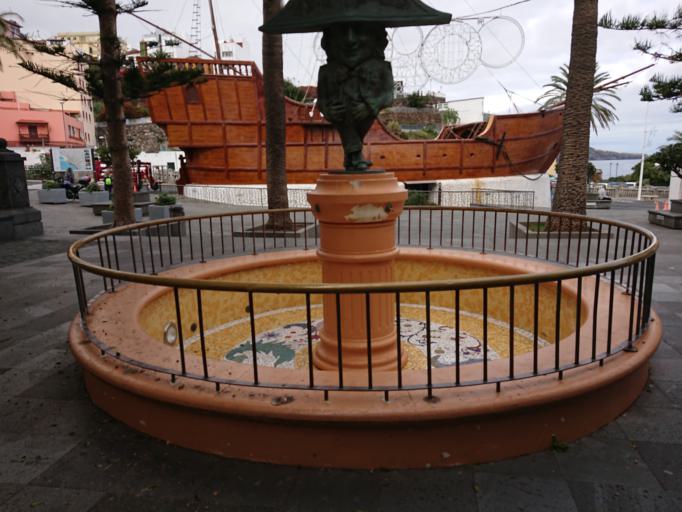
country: ES
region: Canary Islands
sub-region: Provincia de Santa Cruz de Tenerife
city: Santa Cruz de la Palma
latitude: 28.6879
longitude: -17.7612
